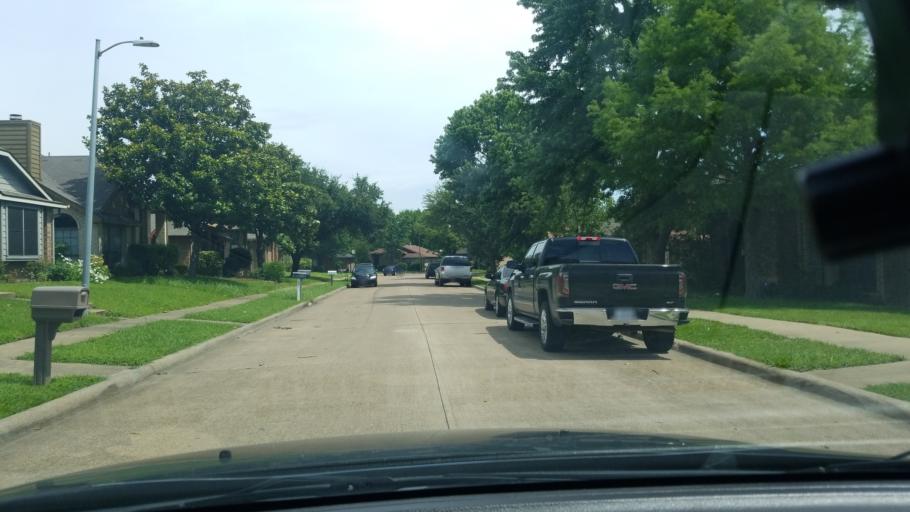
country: US
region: Texas
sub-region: Dallas County
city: Mesquite
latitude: 32.7614
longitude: -96.5796
